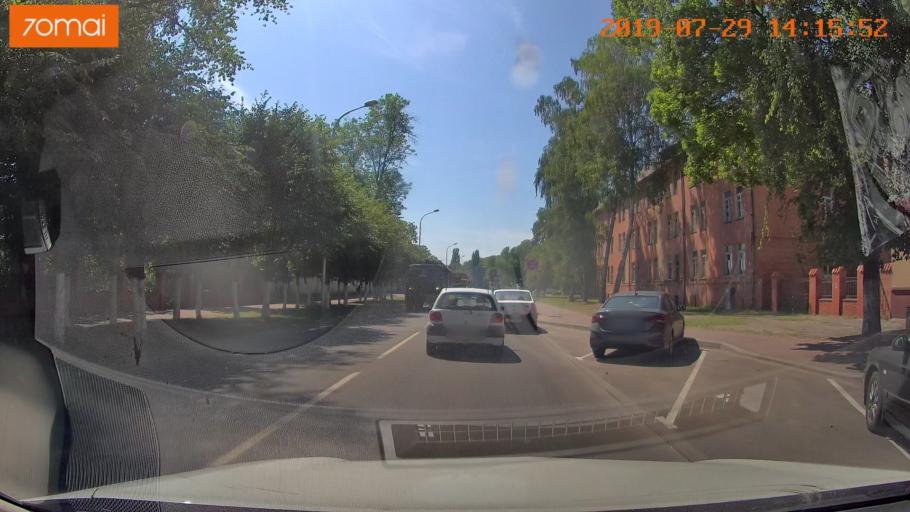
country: RU
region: Kaliningrad
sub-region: Gorod Kaliningrad
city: Baltiysk
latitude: 54.6457
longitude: 19.8977
